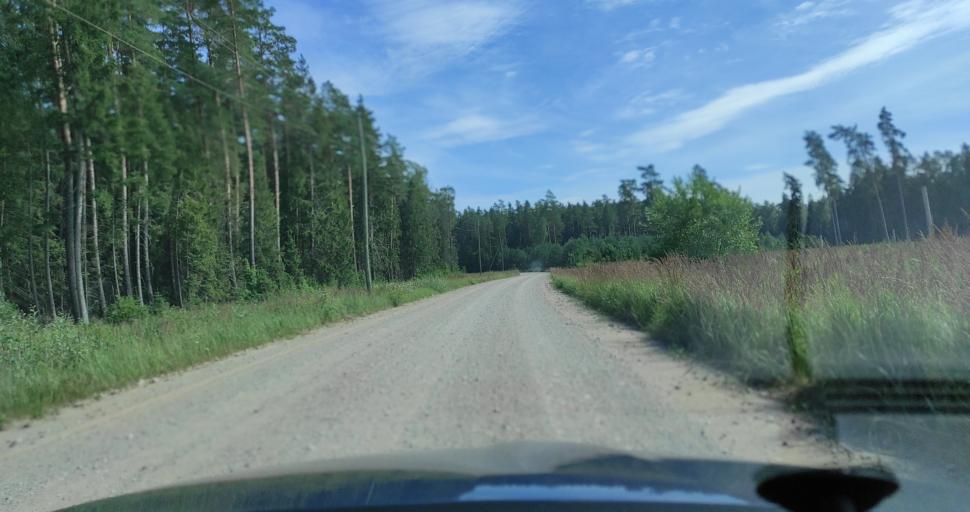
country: LV
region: Durbe
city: Liegi
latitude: 56.7586
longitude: 21.3276
